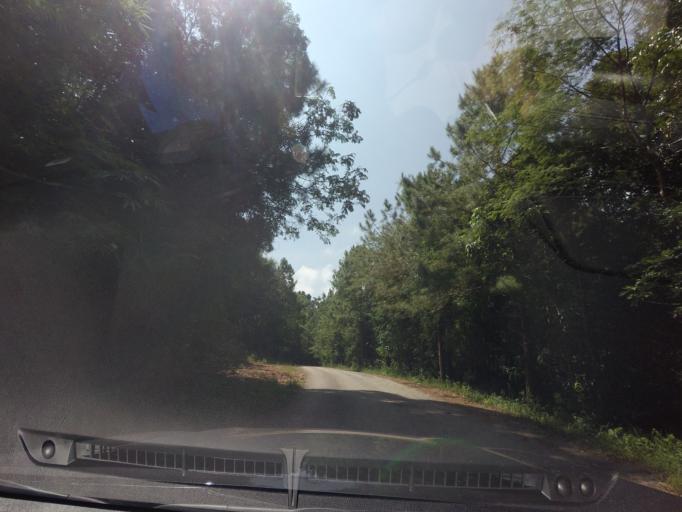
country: TH
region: Loei
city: Na Haeo
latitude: 17.5072
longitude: 100.9408
